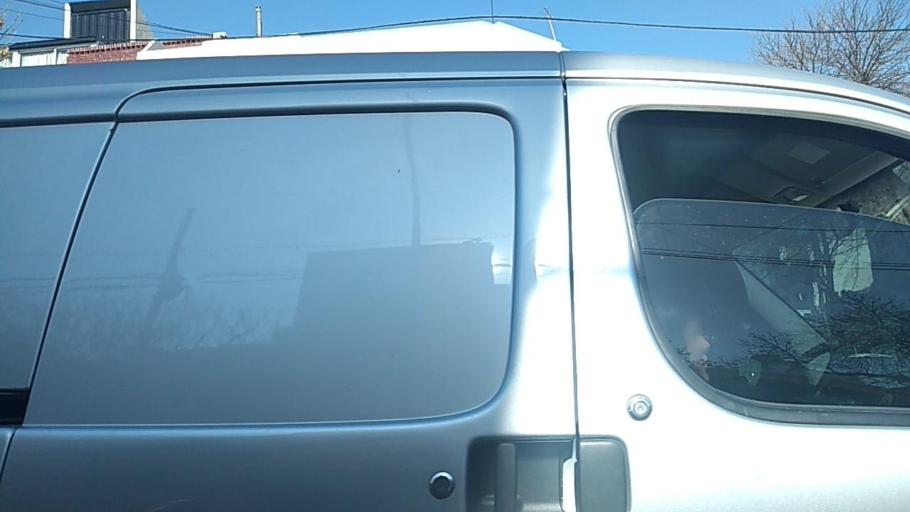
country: AR
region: Buenos Aires F.D.
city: Villa Santa Rita
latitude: -34.6116
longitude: -58.4906
